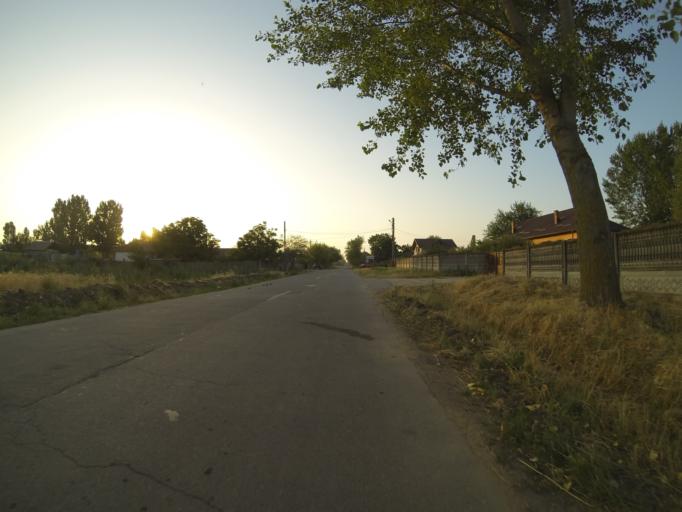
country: RO
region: Dolj
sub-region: Comuna Daneti
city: Brabeti
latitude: 43.9762
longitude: 23.9840
